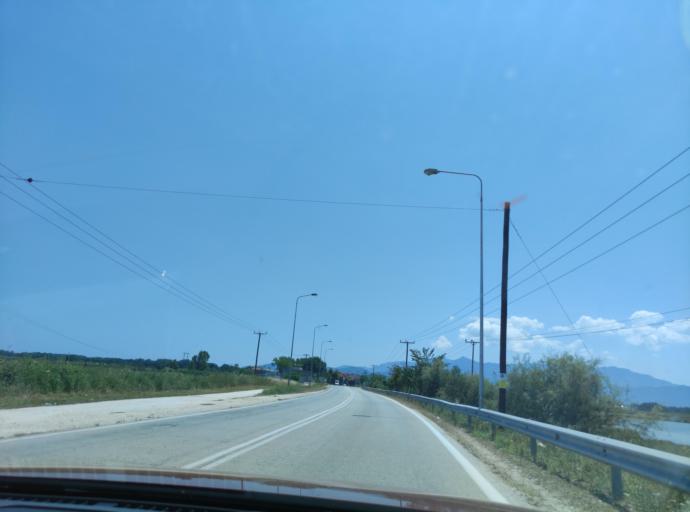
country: GR
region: East Macedonia and Thrace
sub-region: Nomos Kavalas
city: Keramoti
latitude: 40.8670
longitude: 24.7051
